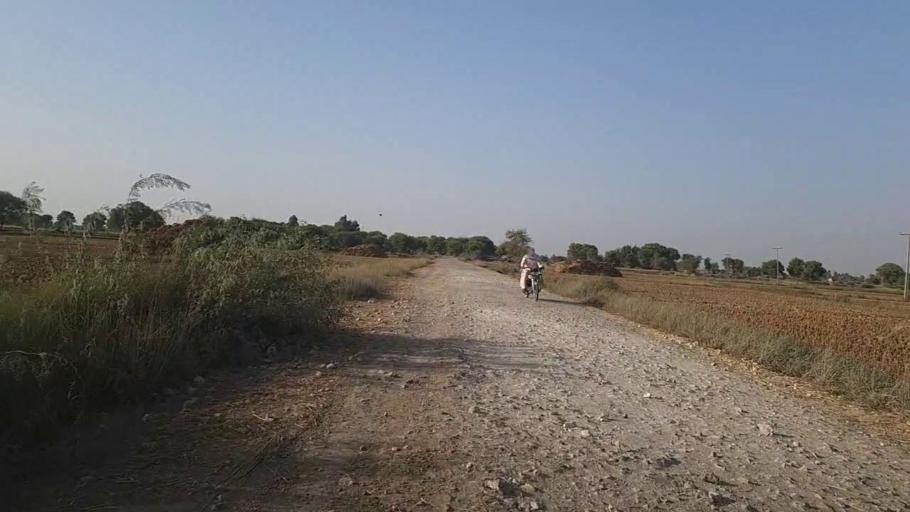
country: PK
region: Sindh
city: Kashmor
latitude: 28.4203
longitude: 69.4087
